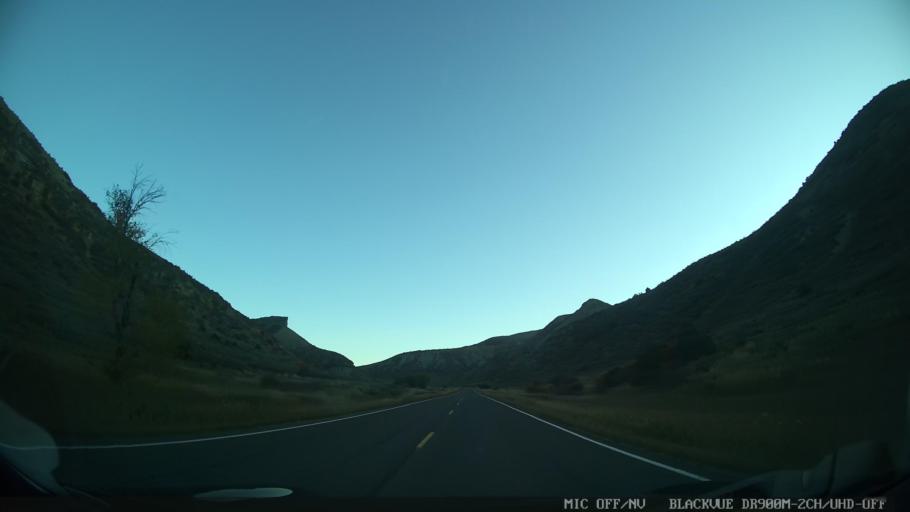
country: US
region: Colorado
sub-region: Eagle County
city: Edwards
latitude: 39.7782
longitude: -106.6814
